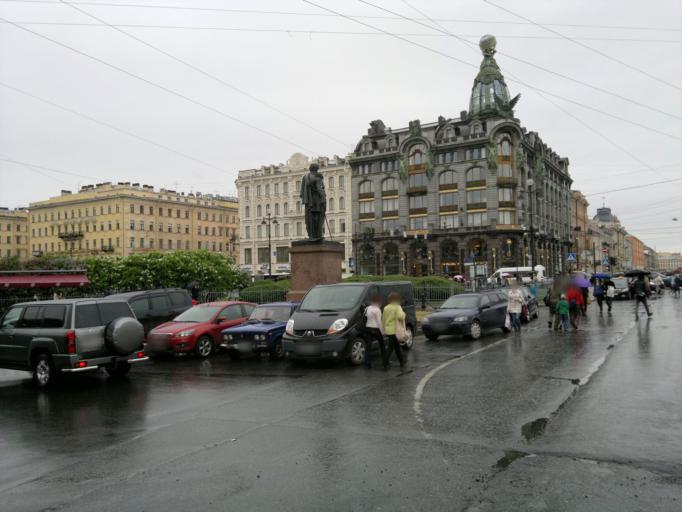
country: RU
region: St.-Petersburg
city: Saint Petersburg
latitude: 59.9348
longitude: 30.3262
